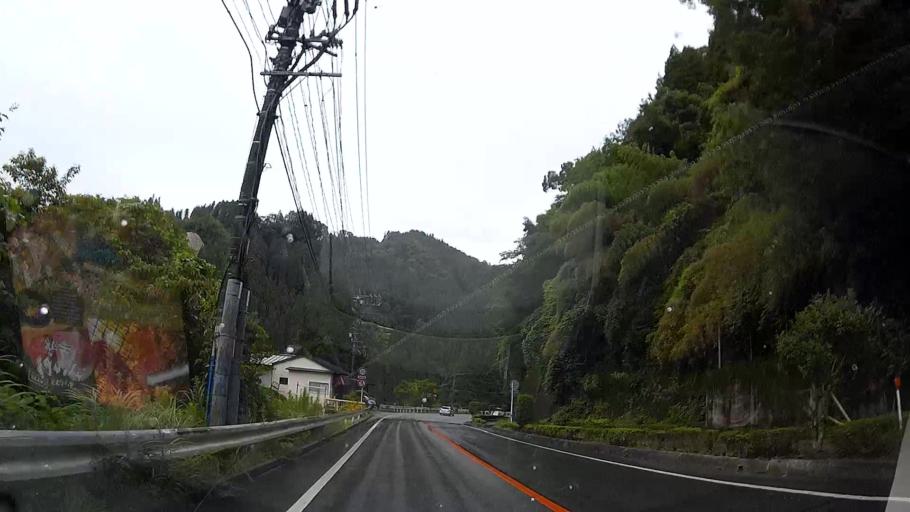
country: JP
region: Oita
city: Tsukawaki
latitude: 33.1583
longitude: 131.0480
